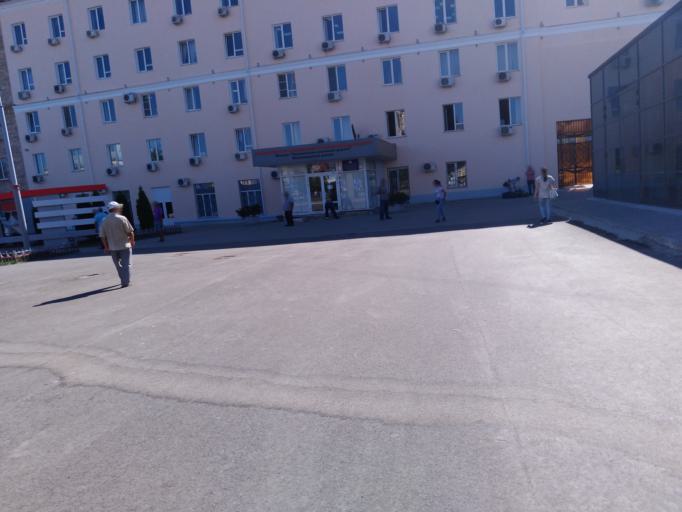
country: RU
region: Volgograd
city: Volgograd
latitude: 48.7120
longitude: 44.5131
